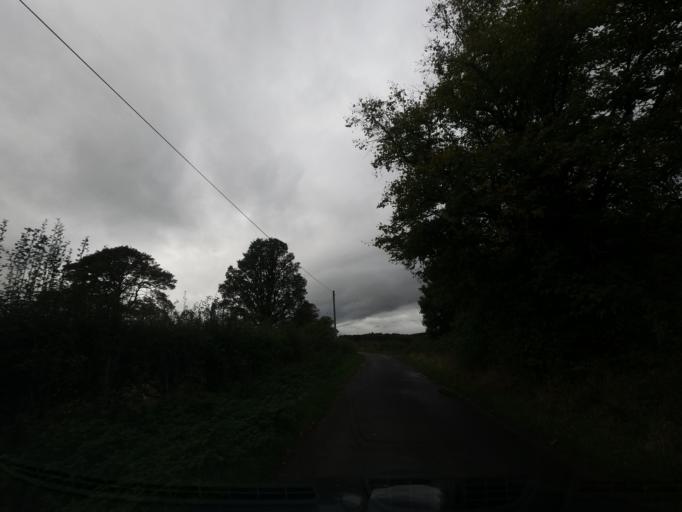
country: GB
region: England
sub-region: Northumberland
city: Doddington
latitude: 55.6004
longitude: -2.0312
